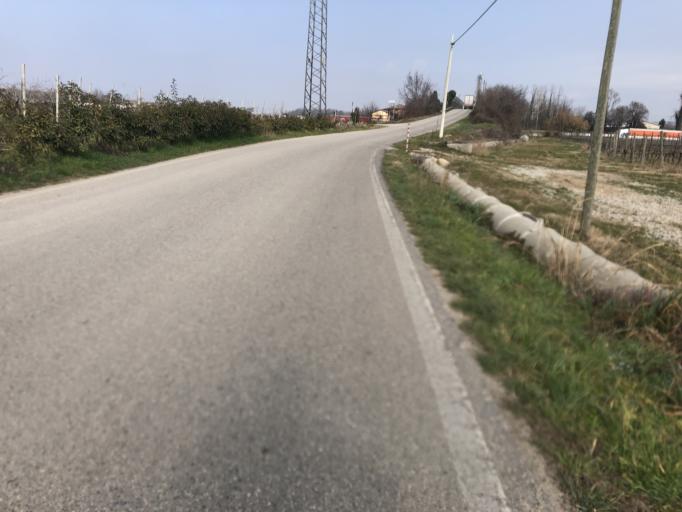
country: IT
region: Veneto
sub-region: Provincia di Verona
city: San Giorgio in Salici
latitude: 45.4158
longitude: 10.7985
